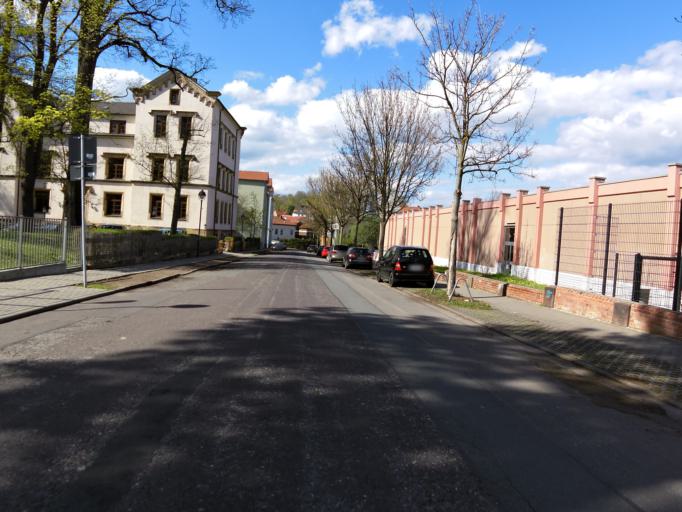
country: DE
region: Thuringia
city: Gotha
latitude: 50.9480
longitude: 10.6945
